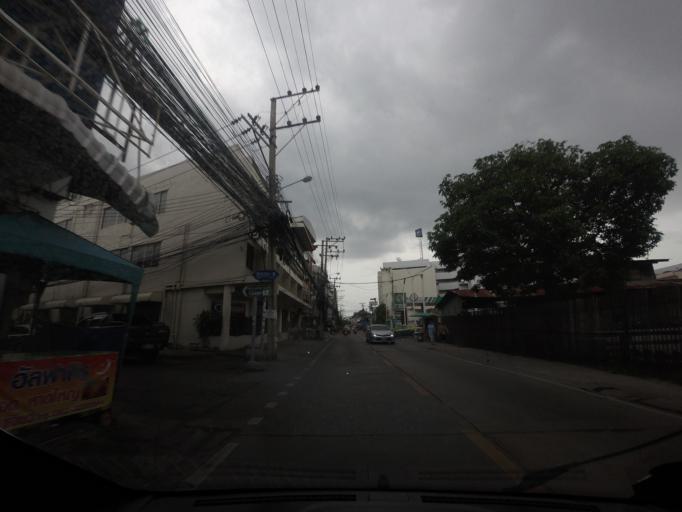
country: TH
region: Bangkok
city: Watthana
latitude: 13.7340
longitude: 100.6076
